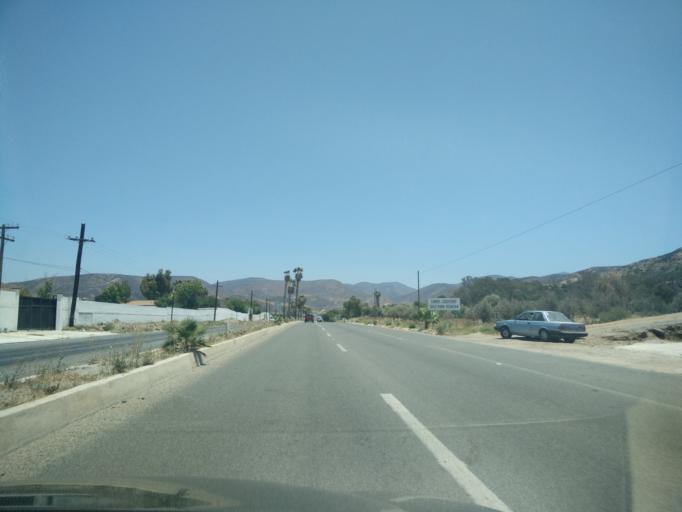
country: MX
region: Baja California
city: El Sauzal
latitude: 31.9095
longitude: -116.6950
